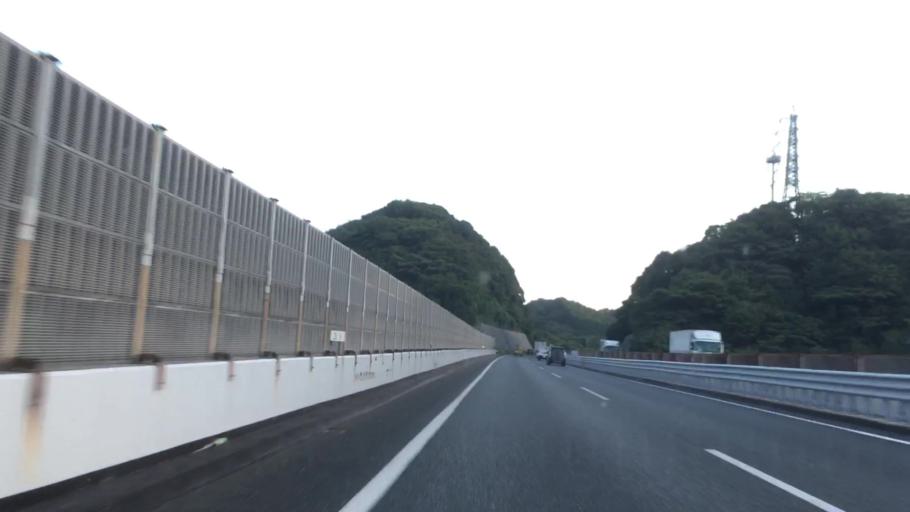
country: JP
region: Yamaguchi
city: Shimonoseki
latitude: 33.8992
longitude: 130.9718
